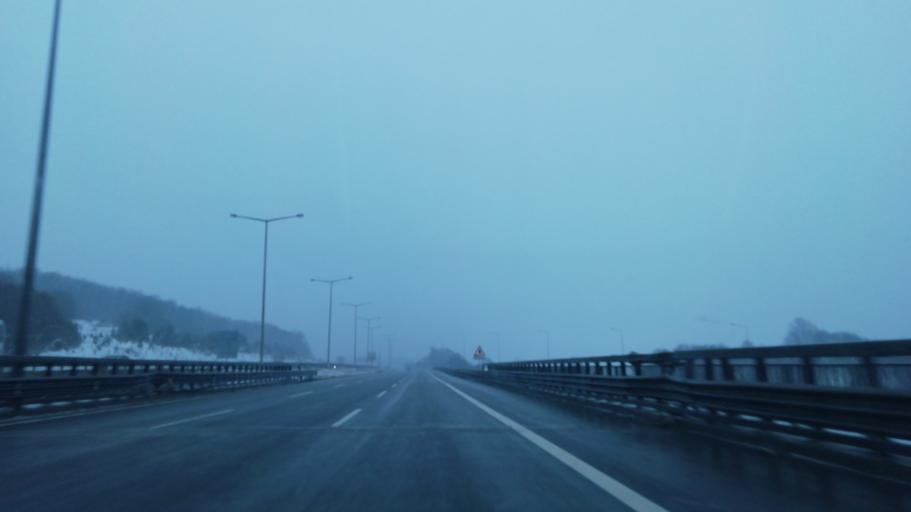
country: TR
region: Bolu
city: Bolu
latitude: 40.7212
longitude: 31.4805
